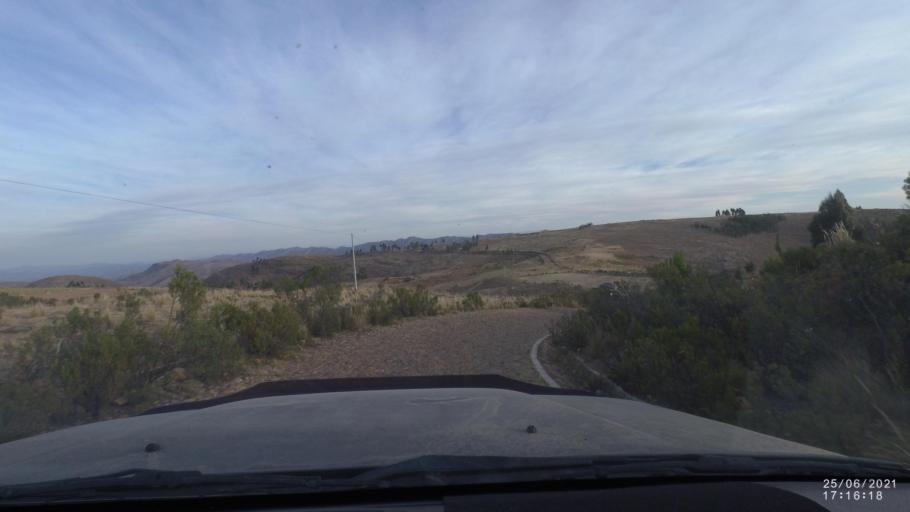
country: BO
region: Cochabamba
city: Arani
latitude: -17.8803
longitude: -65.6996
